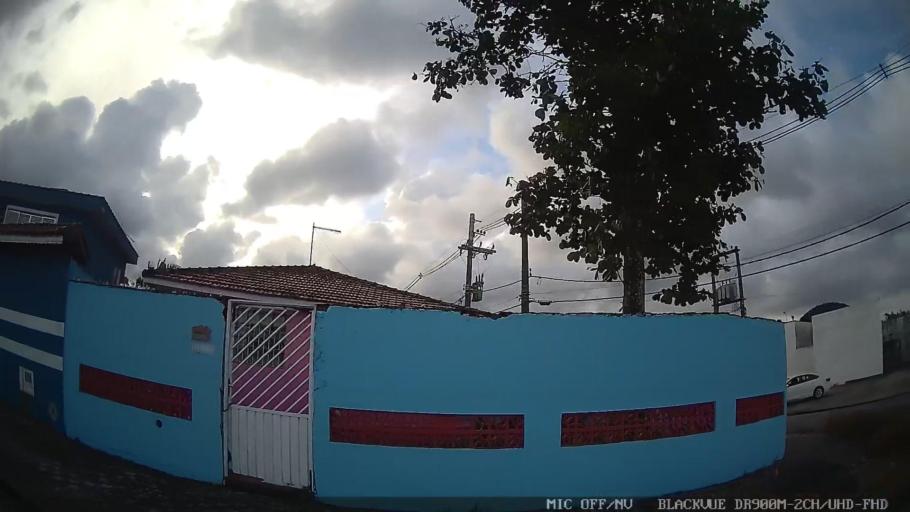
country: BR
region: Sao Paulo
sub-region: Mongagua
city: Mongagua
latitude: -24.1158
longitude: -46.6725
